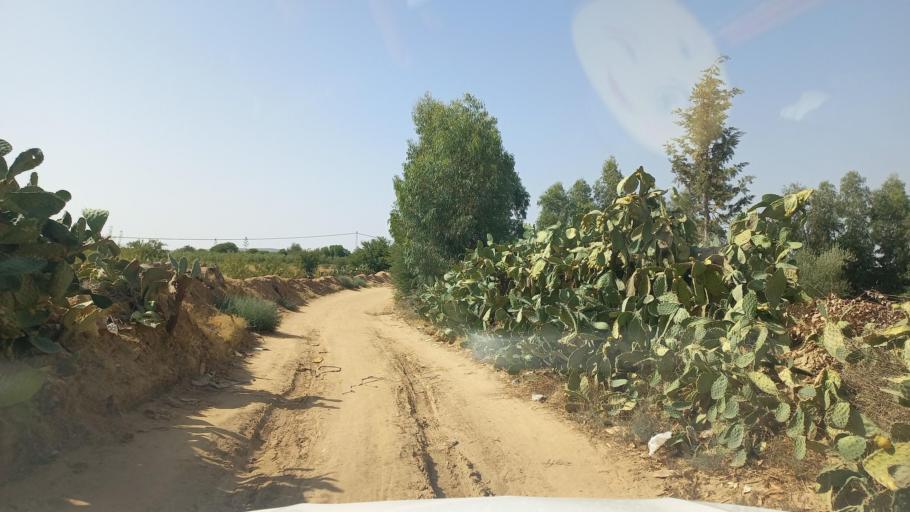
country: TN
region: Al Qasrayn
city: Kasserine
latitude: 35.2459
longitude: 9.0427
